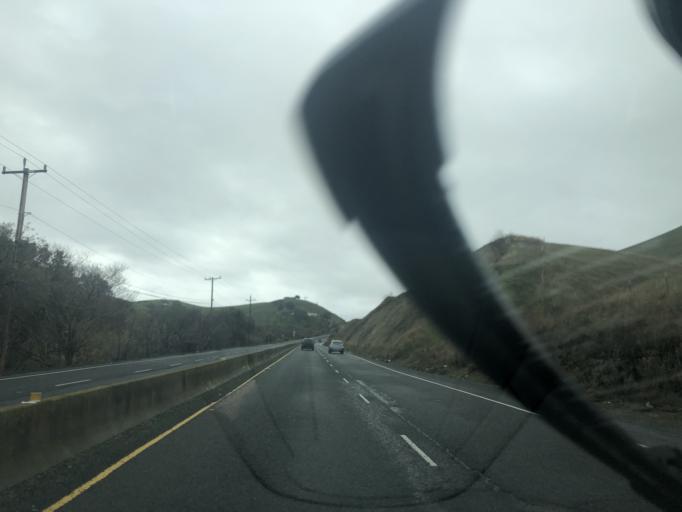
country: US
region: California
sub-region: Contra Costa County
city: Clayton
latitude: 37.9737
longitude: -121.9167
